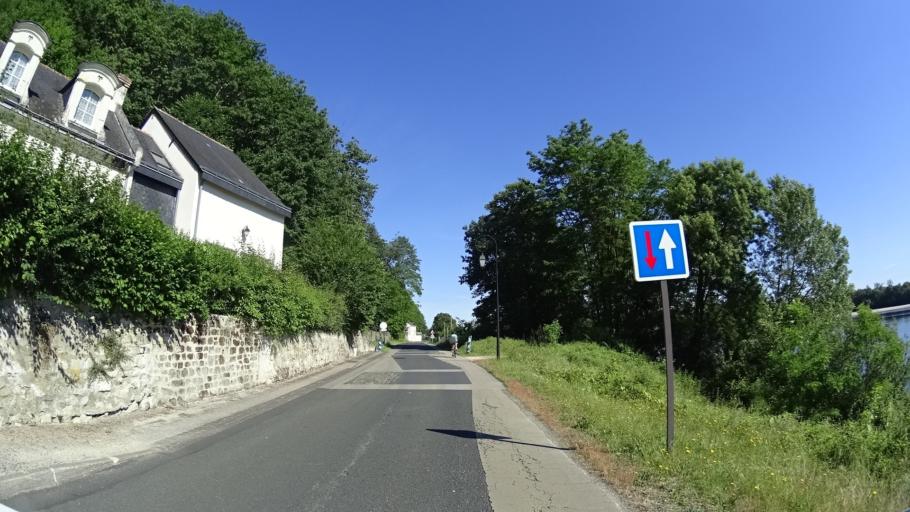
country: FR
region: Pays de la Loire
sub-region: Departement de Maine-et-Loire
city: Saint-Martin-de-la-Place
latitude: 47.3012
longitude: -0.1433
